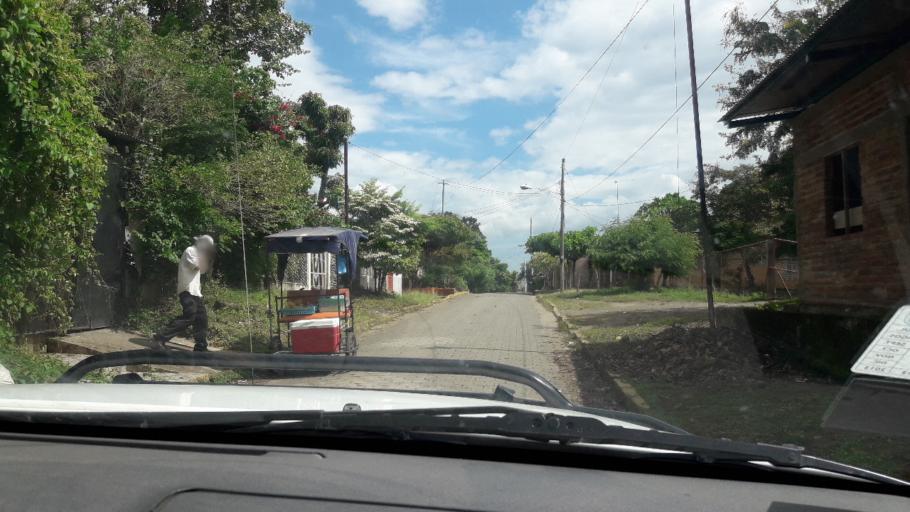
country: NI
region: Rivas
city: Buenos Aires
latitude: 11.4544
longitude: -85.8252
